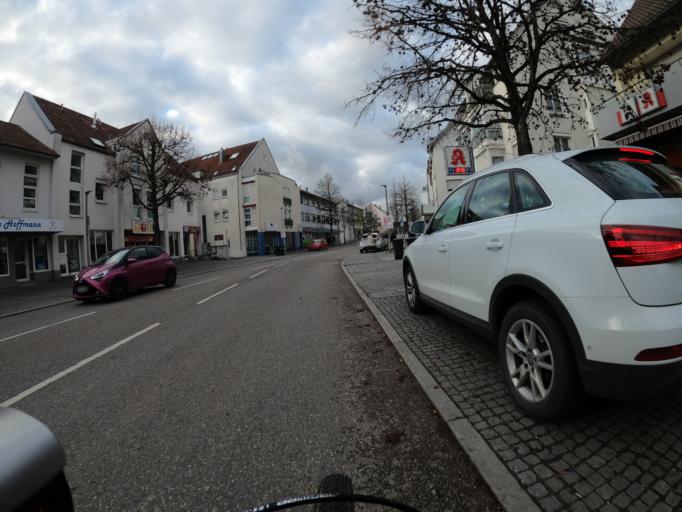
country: DE
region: Baden-Wuerttemberg
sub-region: Regierungsbezirk Stuttgart
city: Wernau
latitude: 48.6895
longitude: 9.4211
